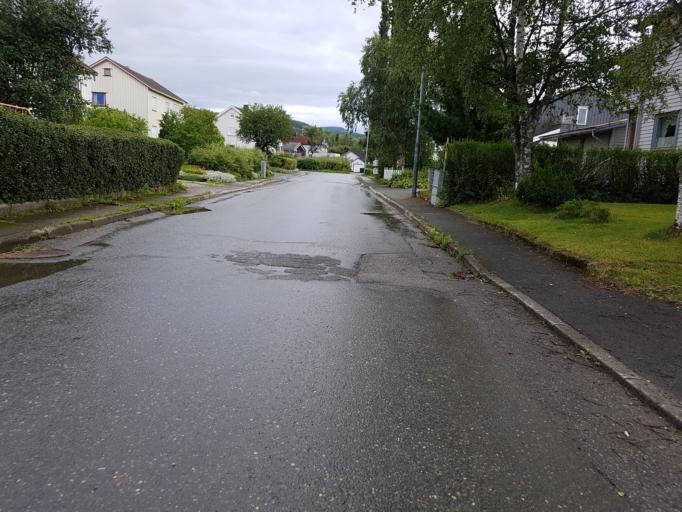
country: NO
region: Sor-Trondelag
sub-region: Trondheim
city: Trondheim
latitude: 63.4049
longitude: 10.4229
